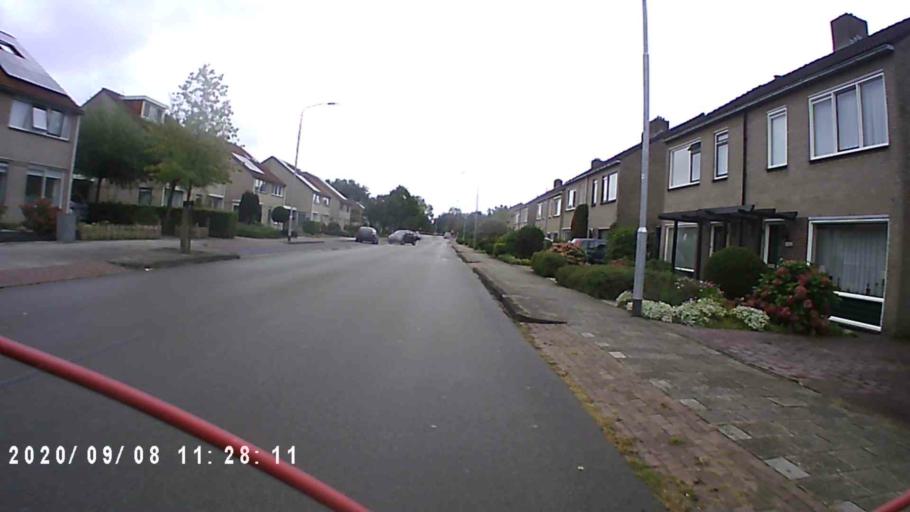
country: NL
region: Groningen
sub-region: Gemeente Hoogezand-Sappemeer
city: Hoogezand
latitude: 53.1622
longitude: 6.7642
